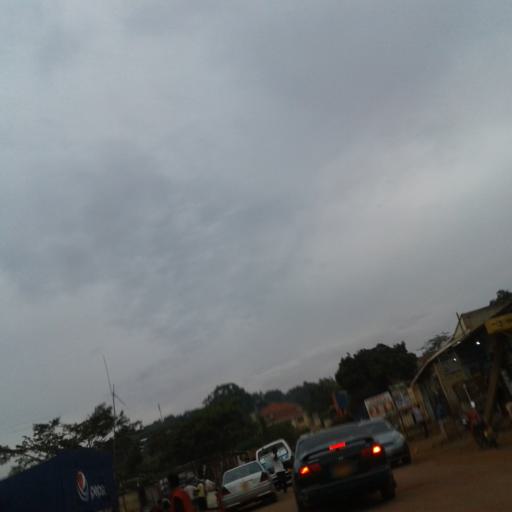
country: UG
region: Central Region
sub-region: Kampala District
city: Kampala
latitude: 0.2470
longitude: 32.6195
